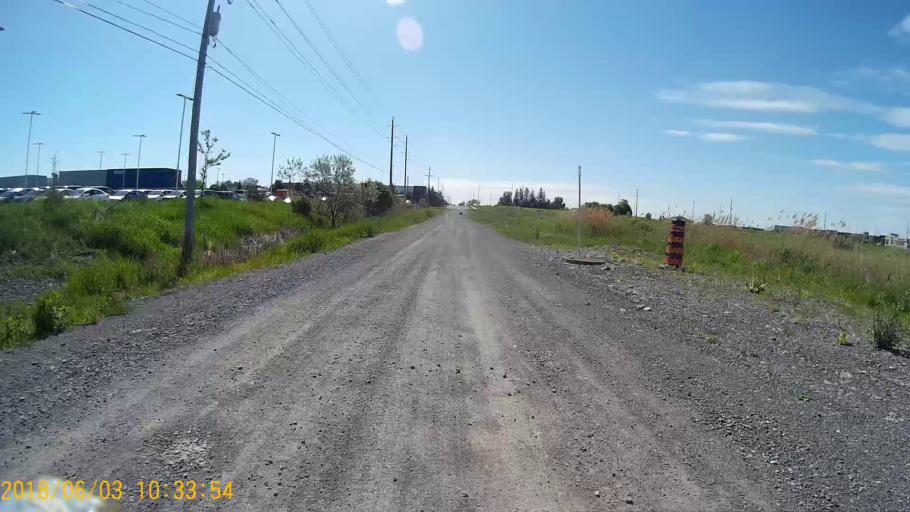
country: CA
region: Ontario
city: Bells Corners
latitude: 45.3087
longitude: -75.9216
